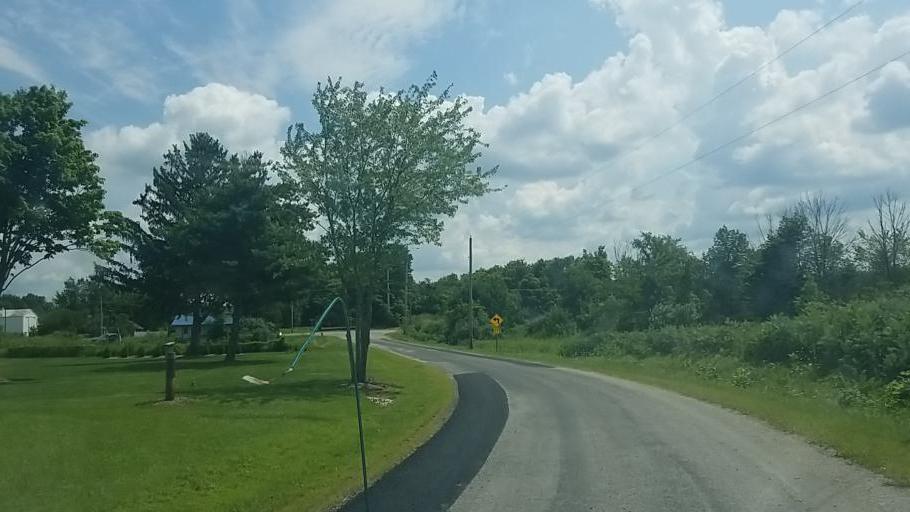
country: US
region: Ohio
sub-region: Wayne County
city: West Salem
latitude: 41.0268
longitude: -82.0791
